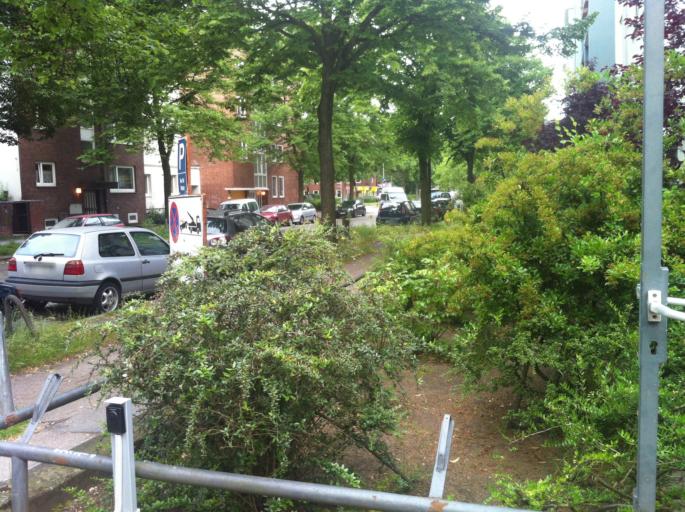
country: DE
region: Hamburg
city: Barmbek-Nord
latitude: 53.5826
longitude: 10.0489
